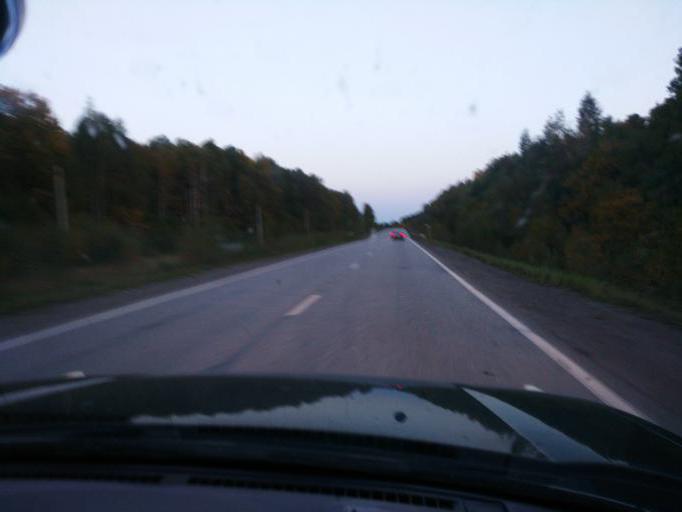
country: RU
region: Perm
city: Verkhnechusovskiye Gorodki
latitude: 58.2675
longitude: 56.9574
